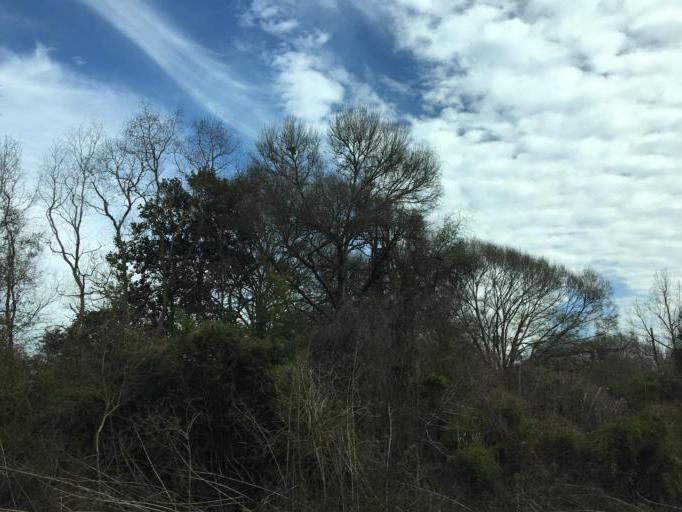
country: US
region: Louisiana
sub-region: Ascension Parish
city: Prairieville
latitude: 30.2949
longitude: -90.9912
